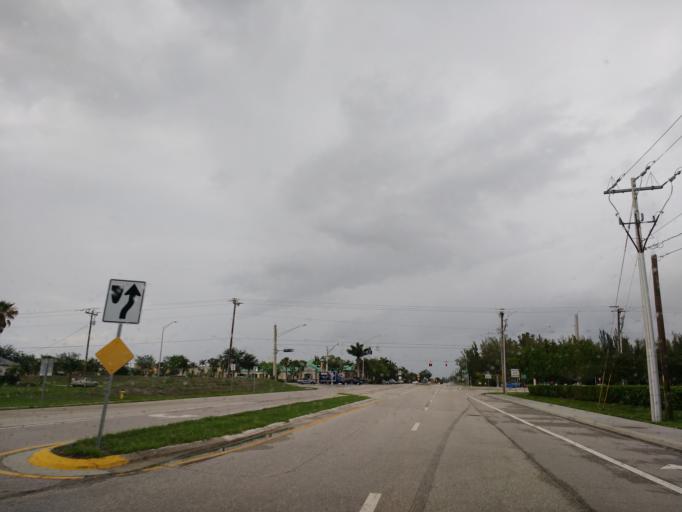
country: US
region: Florida
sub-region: Lee County
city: Cape Coral
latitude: 26.6060
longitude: -82.0233
